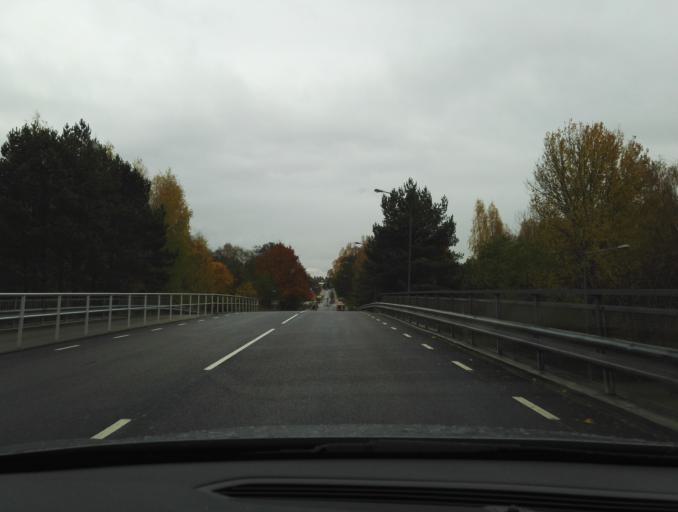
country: SE
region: Kronoberg
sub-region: Vaxjo Kommun
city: Vaexjoe
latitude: 56.8875
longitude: 14.7485
